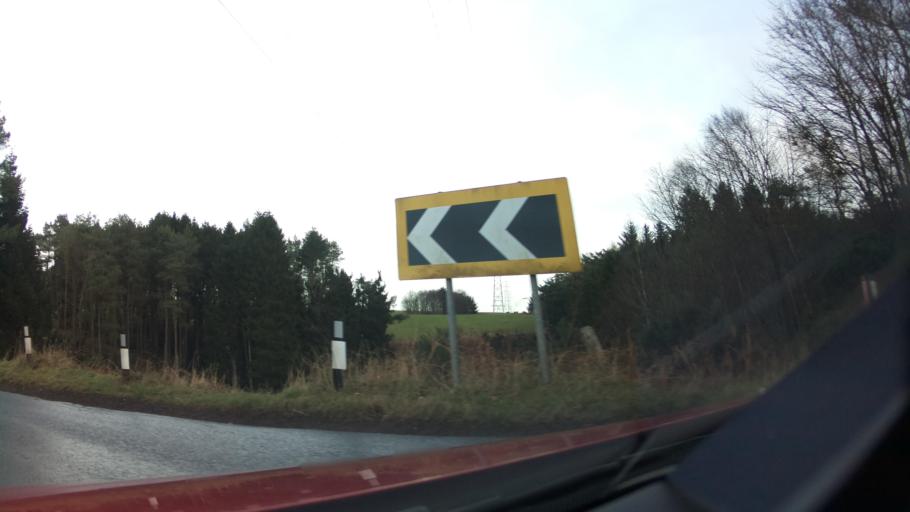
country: GB
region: Scotland
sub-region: Angus
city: Letham
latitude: 56.5503
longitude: -2.7640
